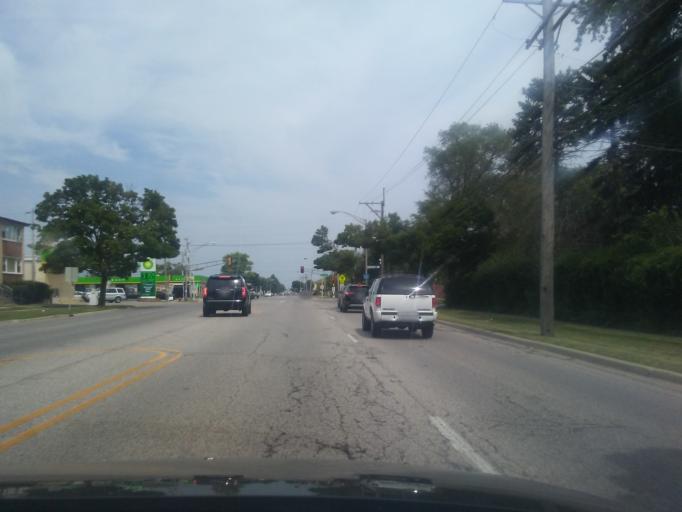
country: US
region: Illinois
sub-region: Cook County
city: Norridge
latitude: 41.9667
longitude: -87.8282
